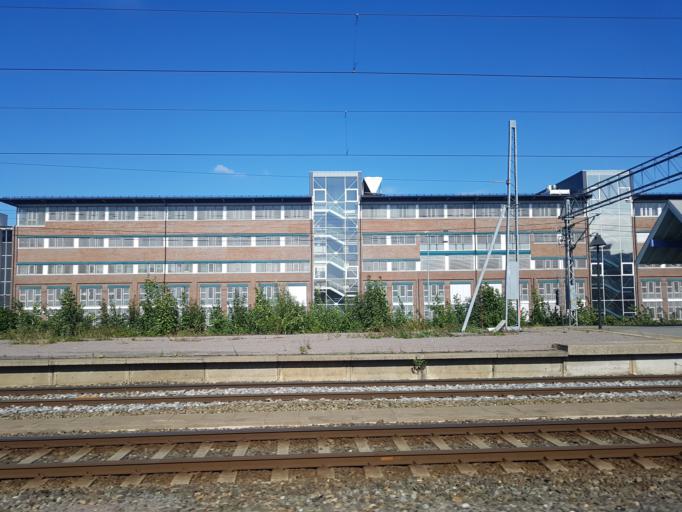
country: NO
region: Oslo
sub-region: Oslo
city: Sjolyststranda
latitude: 59.9232
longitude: 10.6770
